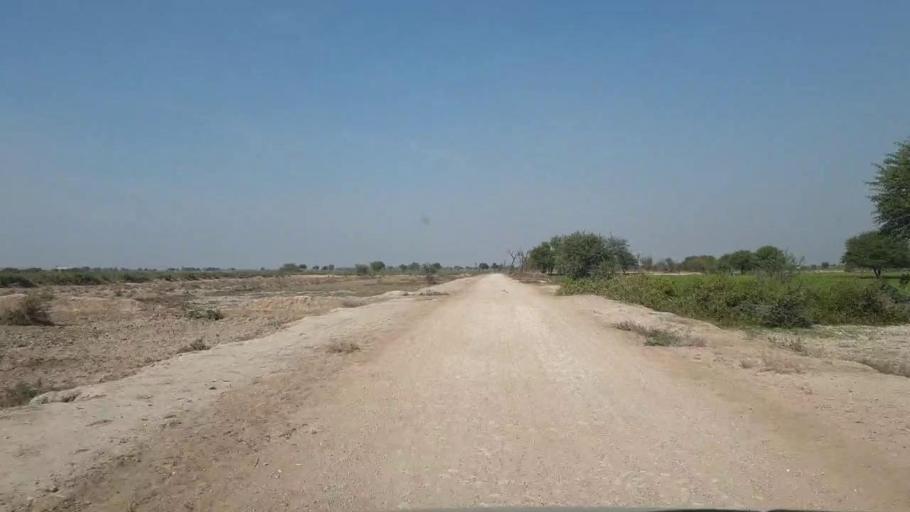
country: PK
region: Sindh
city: Chambar
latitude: 25.3286
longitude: 68.8098
